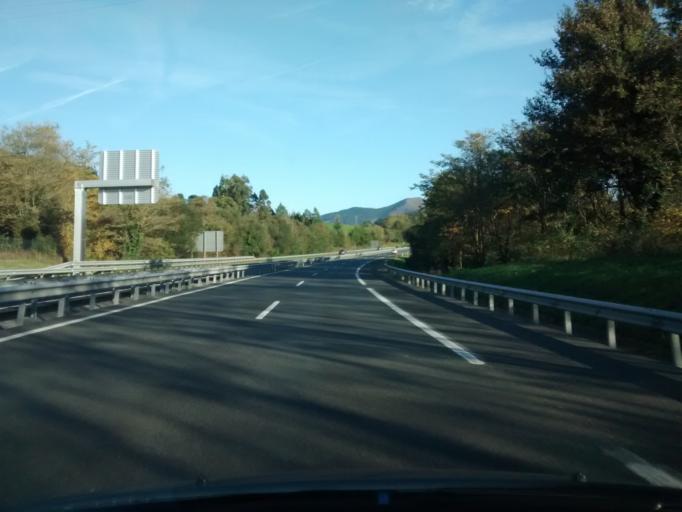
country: ES
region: Basque Country
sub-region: Bizkaia
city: Berriz
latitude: 43.1692
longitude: -2.5855
